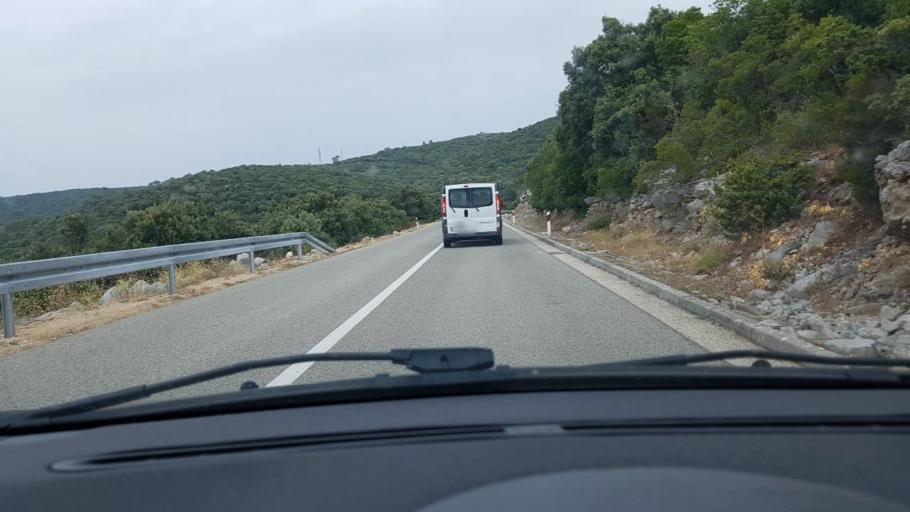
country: HR
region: Dubrovacko-Neretvanska
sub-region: Grad Korcula
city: Zrnovo
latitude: 42.9408
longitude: 17.0072
